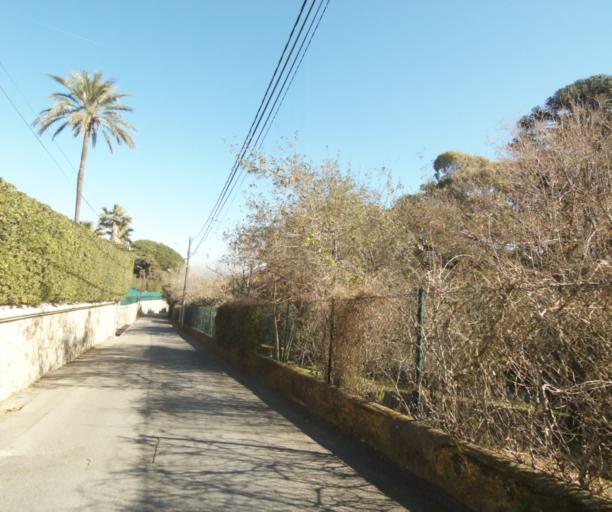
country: FR
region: Provence-Alpes-Cote d'Azur
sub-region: Departement des Alpes-Maritimes
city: Antibes
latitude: 43.5647
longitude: 7.1236
